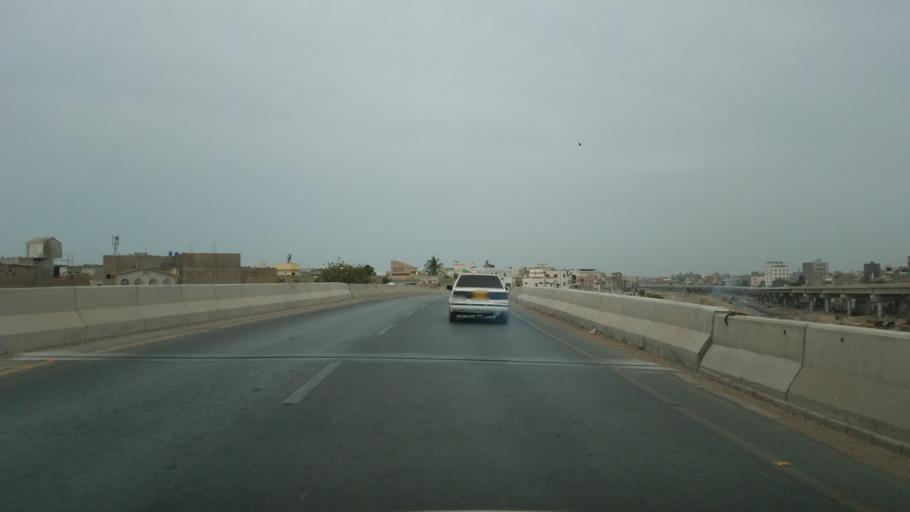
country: PK
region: Sindh
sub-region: Karachi District
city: Karachi
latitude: 24.8990
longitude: 67.0603
